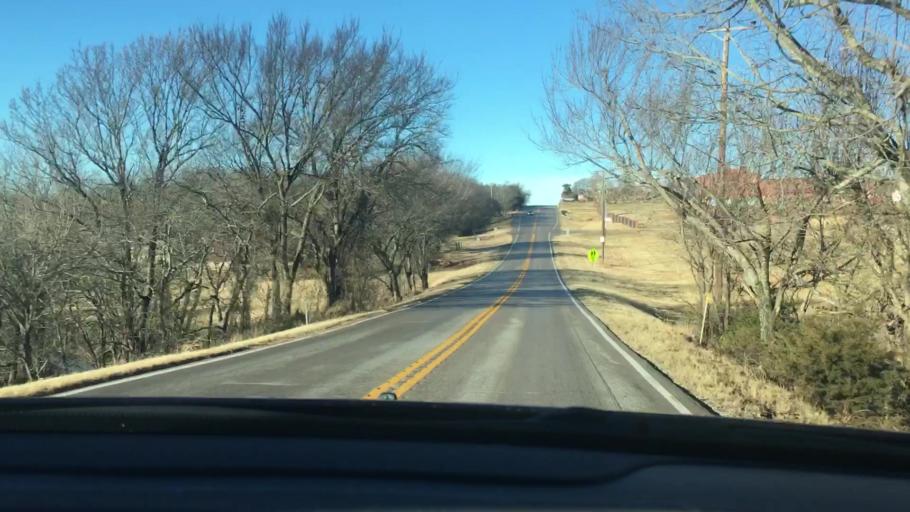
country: US
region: Oklahoma
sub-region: Murray County
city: Sulphur
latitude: 34.5110
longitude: -96.9478
